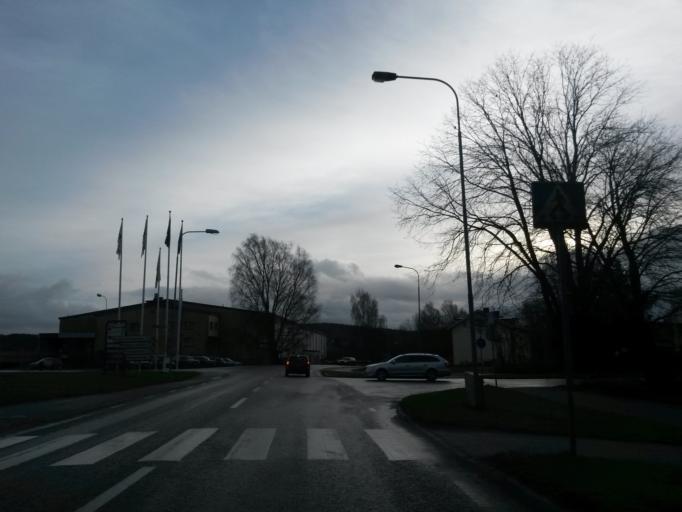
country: SE
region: Vaestra Goetaland
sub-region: Marks Kommun
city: Kinna
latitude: 57.4857
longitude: 12.6476
